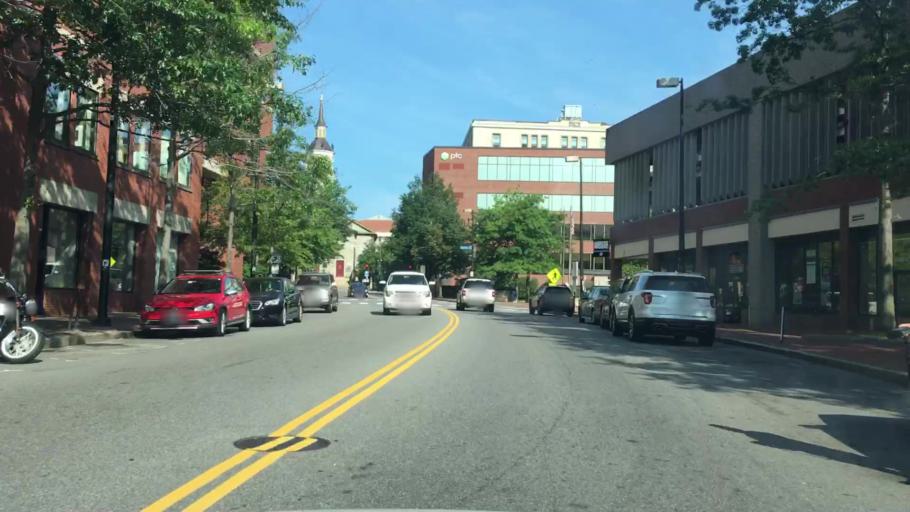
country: US
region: Maine
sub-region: Cumberland County
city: Portland
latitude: 43.6575
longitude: -70.2566
